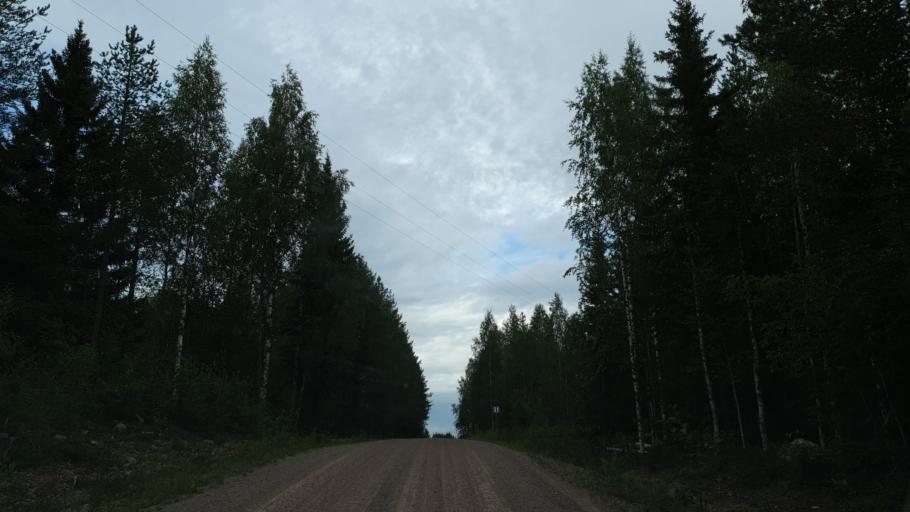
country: FI
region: Kainuu
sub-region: Kehys-Kainuu
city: Suomussalmi
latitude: 64.4531
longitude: 28.9759
